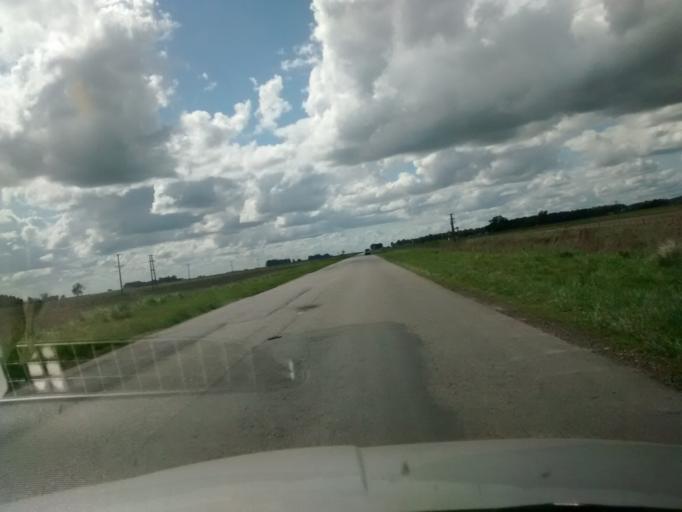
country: AR
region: Buenos Aires
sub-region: Partido de Loberia
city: Loberia
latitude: -37.7024
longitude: -58.7250
